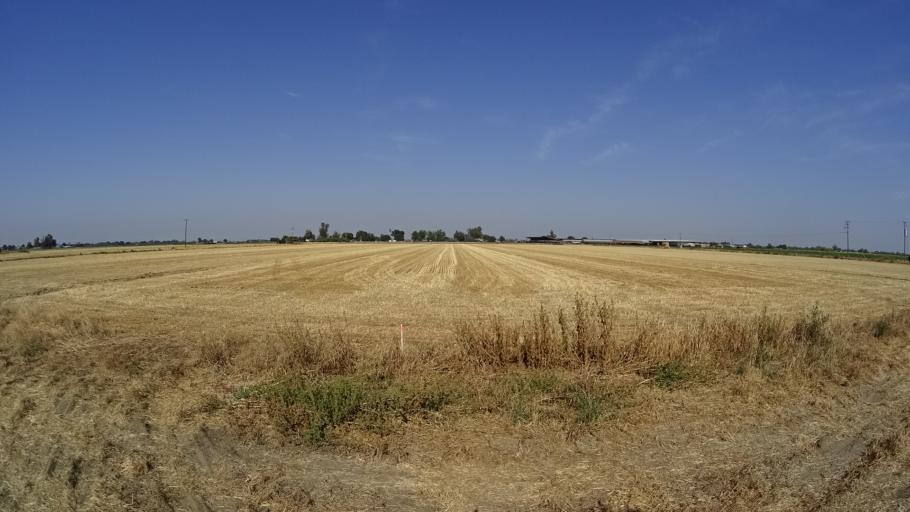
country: US
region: California
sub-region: Fresno County
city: Riverdale
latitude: 36.3738
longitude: -119.8341
